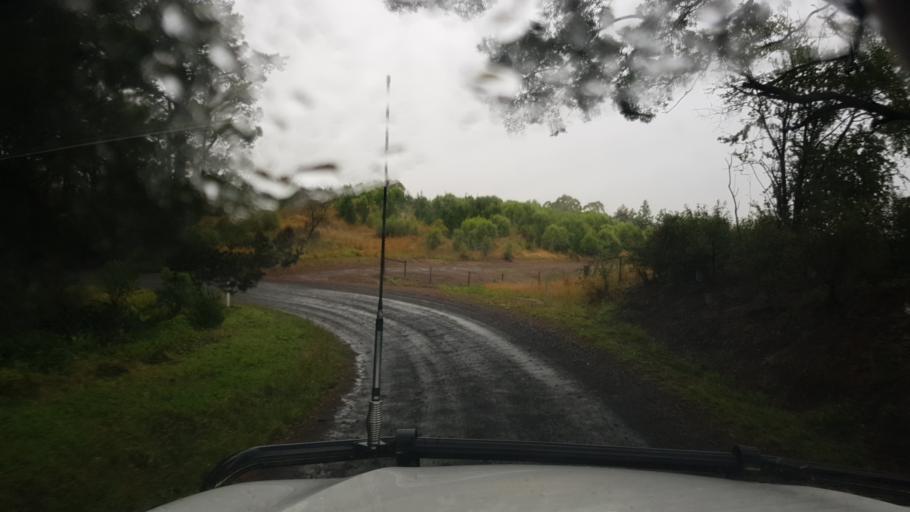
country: AU
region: Victoria
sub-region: Baw Baw
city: Warragul
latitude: -38.2695
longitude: 146.0186
